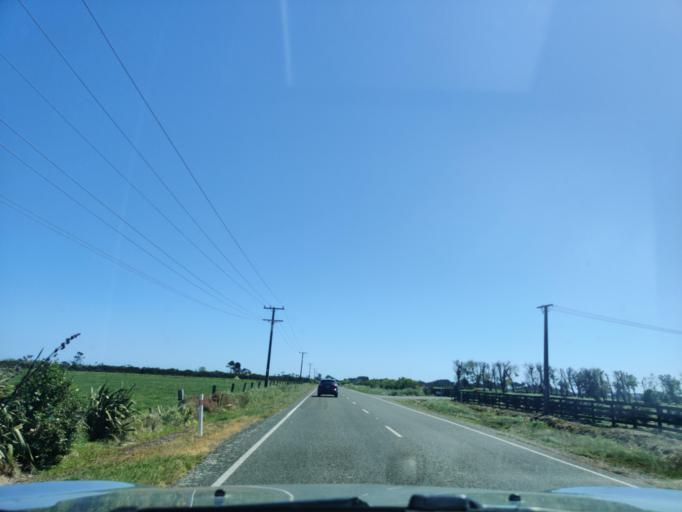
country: NZ
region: Taranaki
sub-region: South Taranaki District
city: Hawera
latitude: -39.5471
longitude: 174.0891
